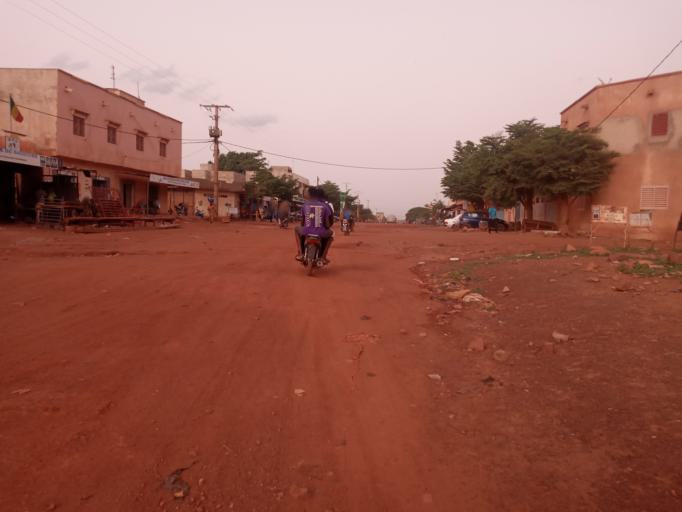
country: ML
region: Bamako
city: Bamako
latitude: 12.5580
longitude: -7.9867
